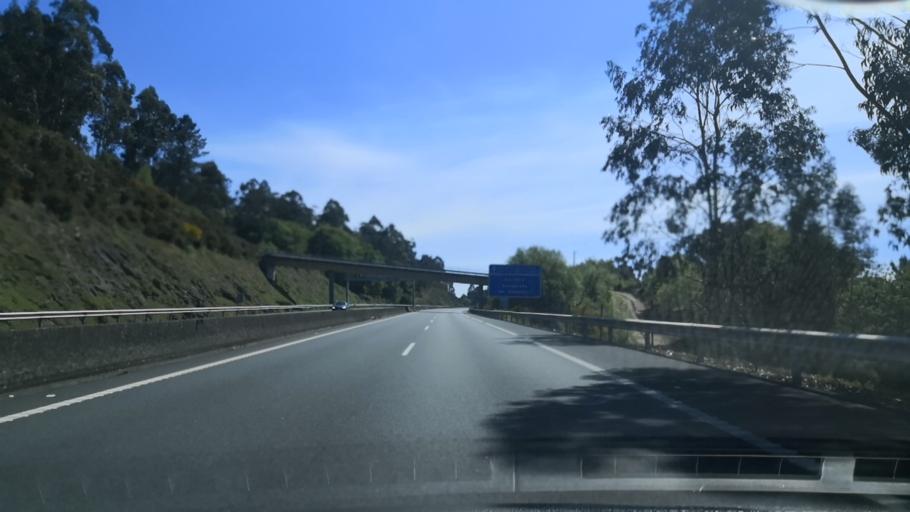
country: ES
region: Galicia
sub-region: Provincia da Coruna
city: Santiago de Compostela
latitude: 42.8501
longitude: -8.5713
